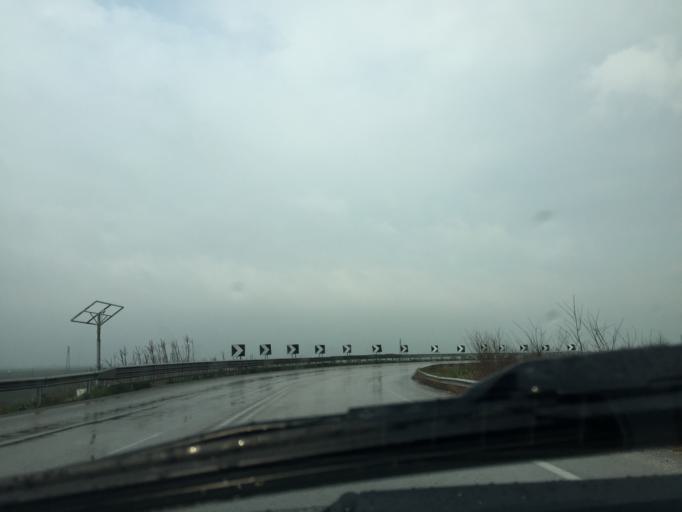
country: IT
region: Apulia
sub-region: Provincia di Foggia
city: Foggia
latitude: 41.4978
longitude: 15.5186
